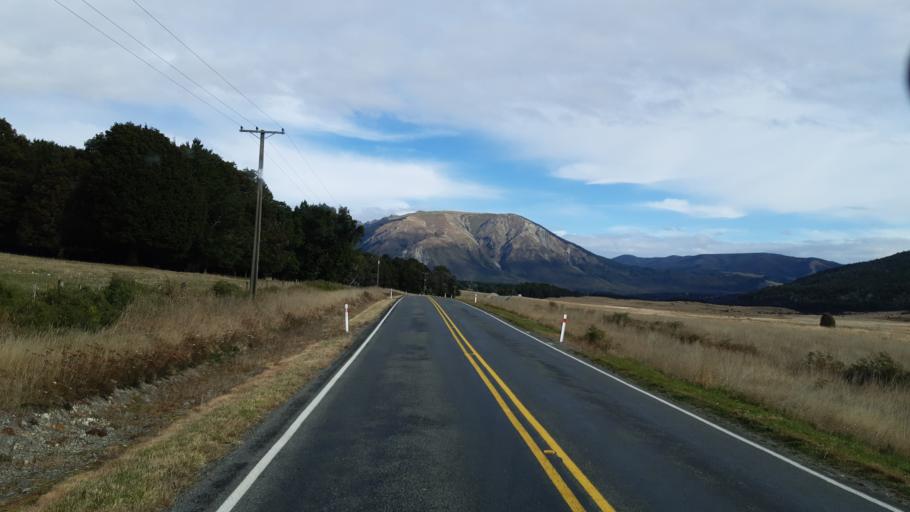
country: NZ
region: Tasman
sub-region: Tasman District
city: Wakefield
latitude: -41.7925
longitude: 172.8794
